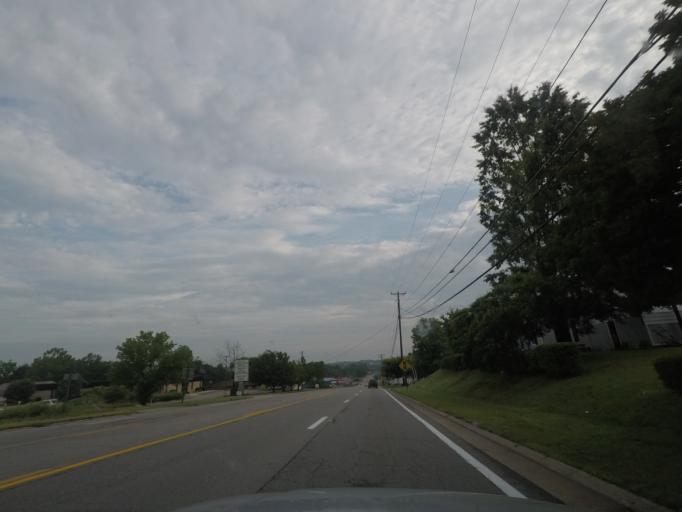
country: US
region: Virginia
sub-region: Halifax County
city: South Boston
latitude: 36.6830
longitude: -78.8990
